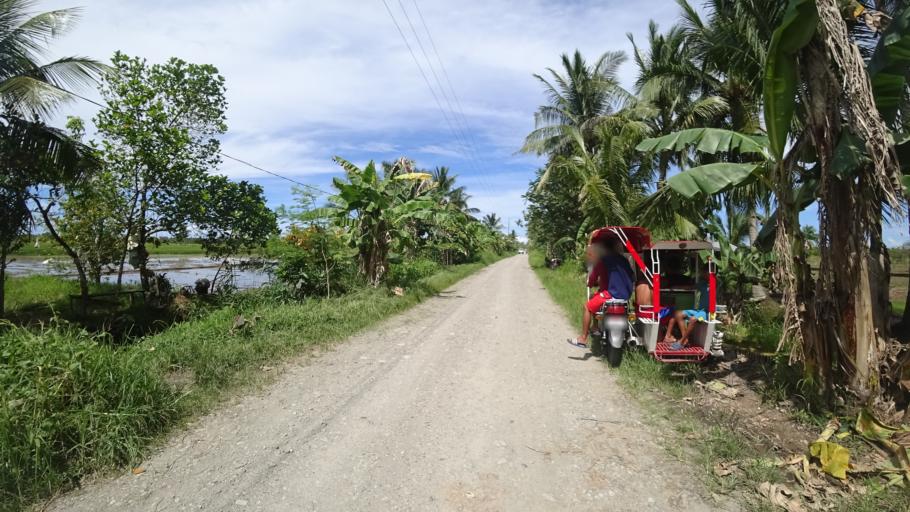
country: PH
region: Eastern Visayas
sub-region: Province of Leyte
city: Liberty
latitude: 10.8593
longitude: 124.9830
